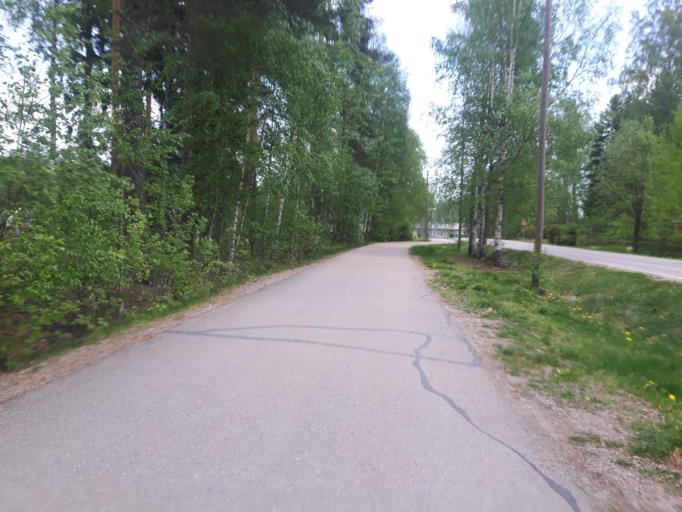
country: FI
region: Uusimaa
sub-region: Porvoo
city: Porvoo
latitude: 60.4016
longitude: 25.7007
